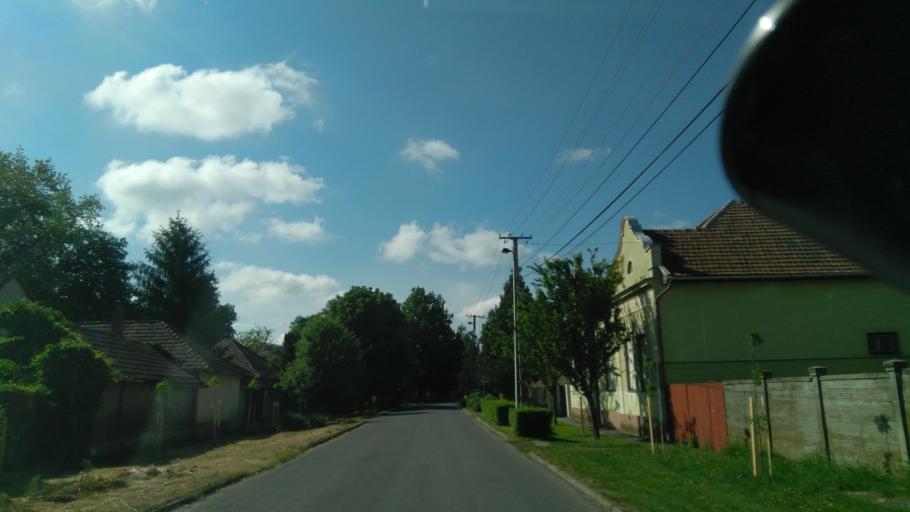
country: HU
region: Bekes
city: Bekes
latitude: 46.7762
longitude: 21.1274
